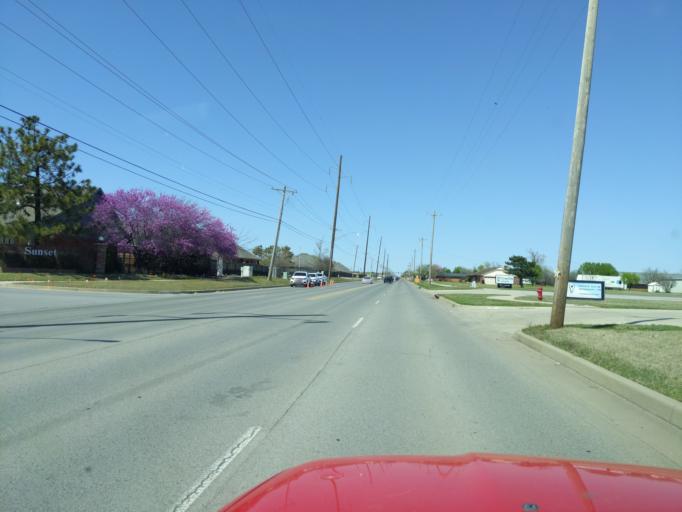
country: US
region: Oklahoma
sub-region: Cleveland County
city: Moore
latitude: 35.3290
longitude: -97.5120
